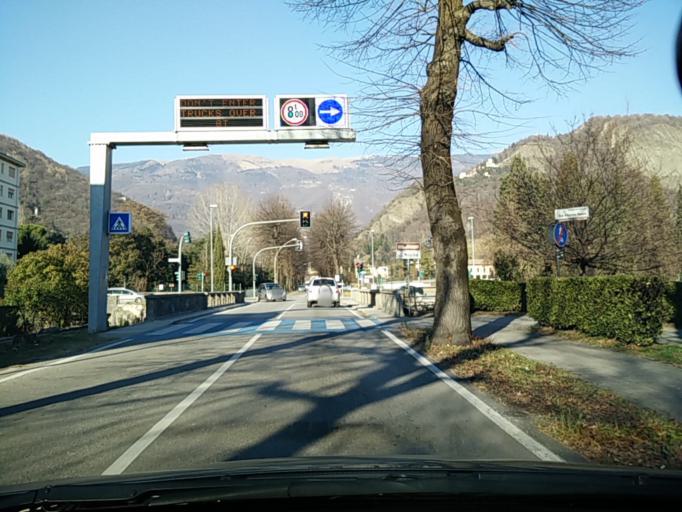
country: IT
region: Veneto
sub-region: Provincia di Treviso
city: Vittorio Veneto
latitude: 45.9941
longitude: 12.2957
